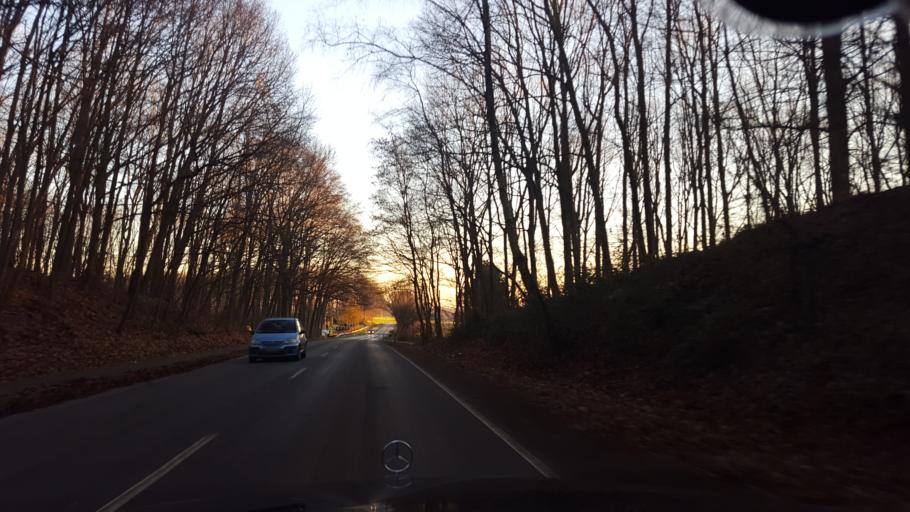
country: DE
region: North Rhine-Westphalia
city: Oer-Erkenschwick
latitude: 51.6609
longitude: 7.2699
